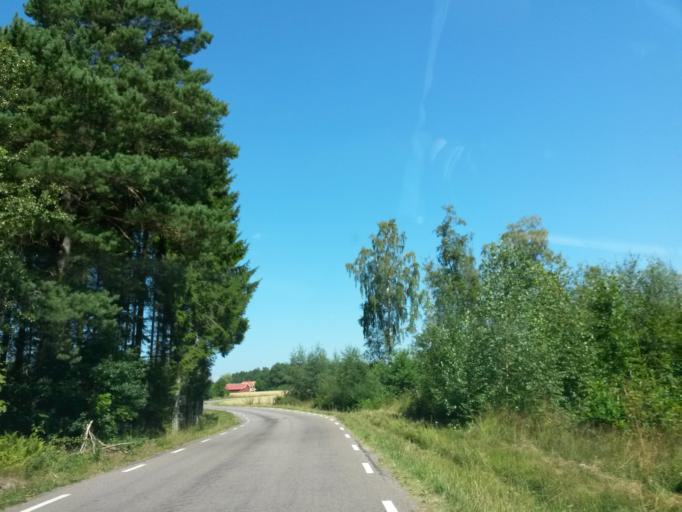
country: SE
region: Vaestra Goetaland
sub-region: Grastorps Kommun
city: Graestorp
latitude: 58.3486
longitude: 12.7758
